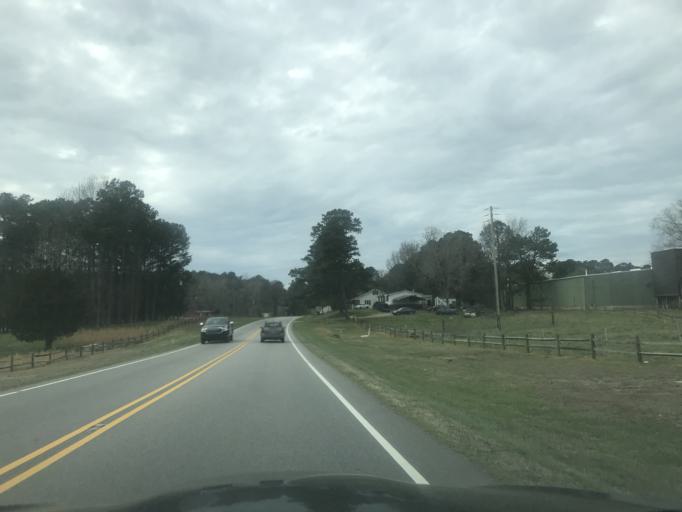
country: US
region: North Carolina
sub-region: Franklin County
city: Franklinton
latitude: 36.0959
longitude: -78.4179
